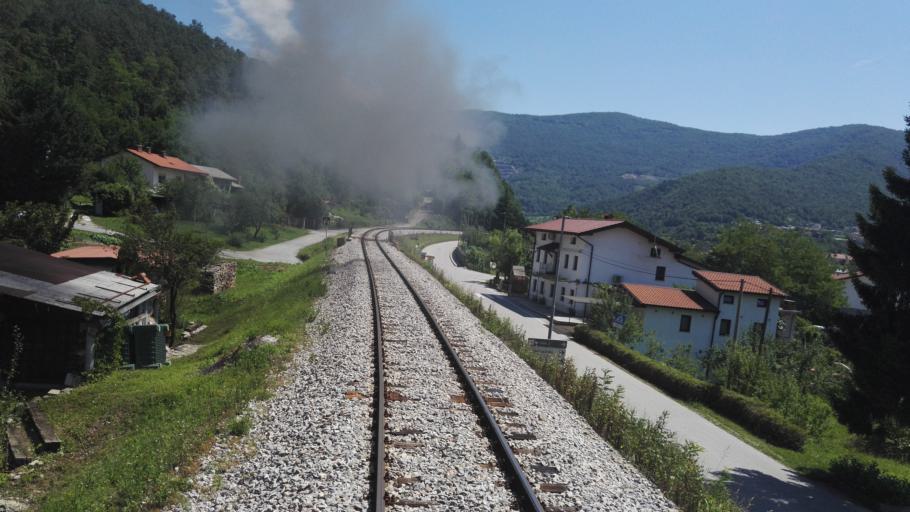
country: SI
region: Kanal
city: Deskle
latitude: 46.0530
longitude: 13.6038
